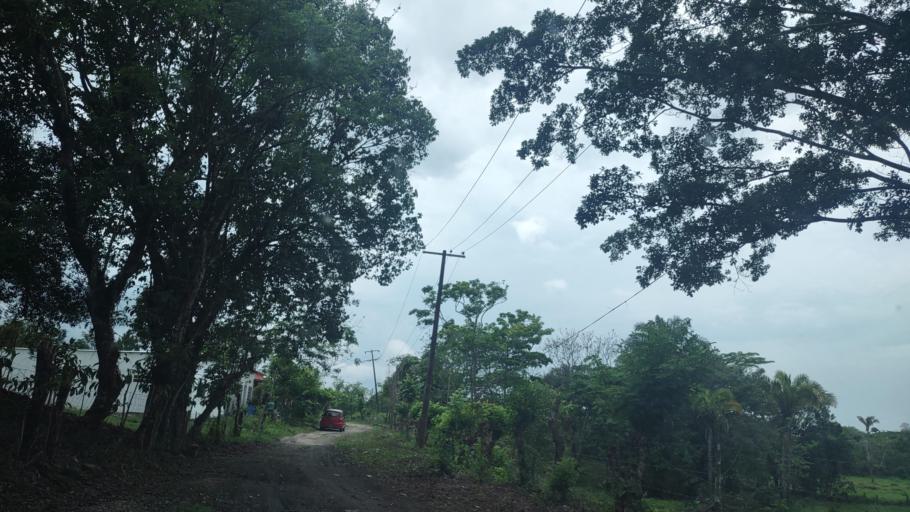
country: MX
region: Veracruz
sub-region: Uxpanapa
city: Poblado 10
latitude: 17.5042
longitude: -94.1622
